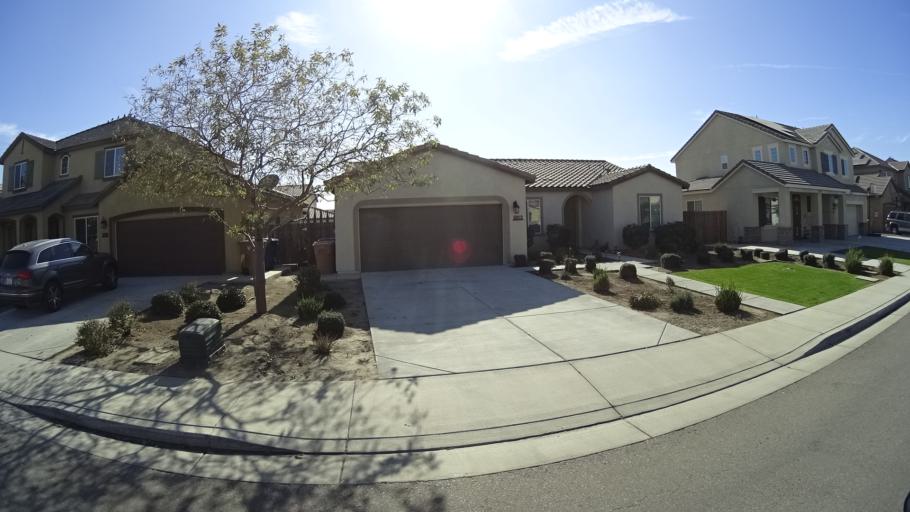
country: US
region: California
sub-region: Kern County
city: Greenfield
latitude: 35.2851
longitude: -119.0585
